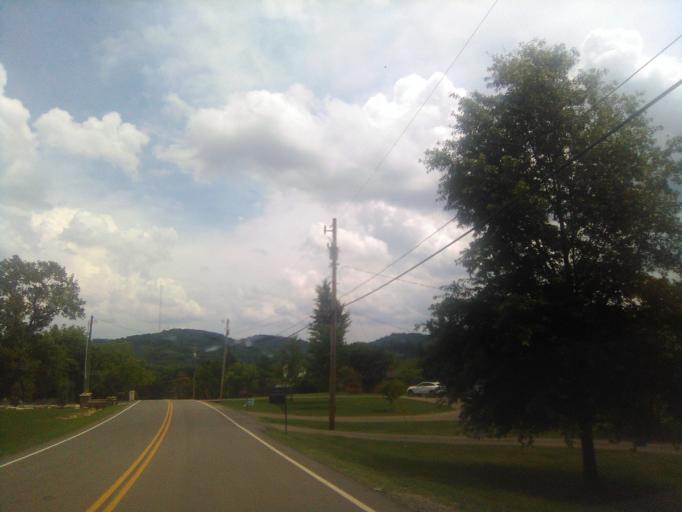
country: US
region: Tennessee
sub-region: Davidson County
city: Forest Hills
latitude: 36.0645
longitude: -86.8514
